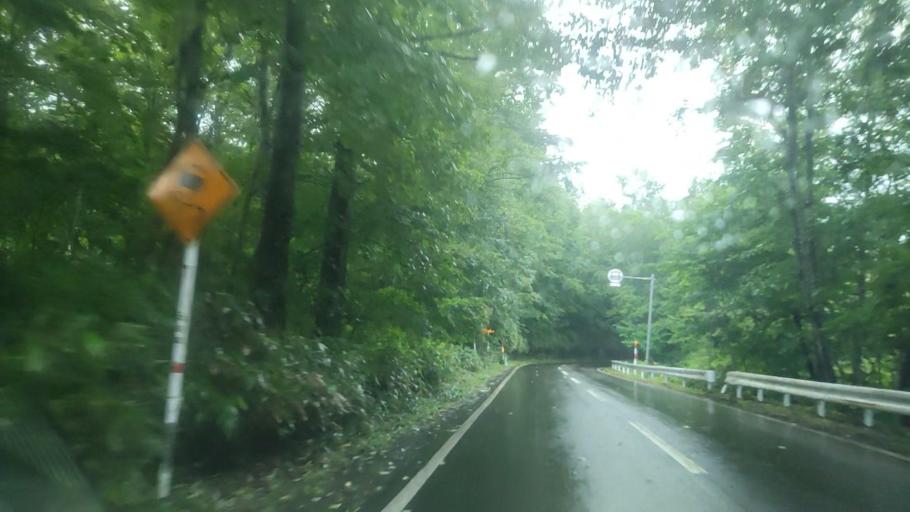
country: JP
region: Hokkaido
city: Muroran
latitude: 42.5223
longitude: 141.1113
